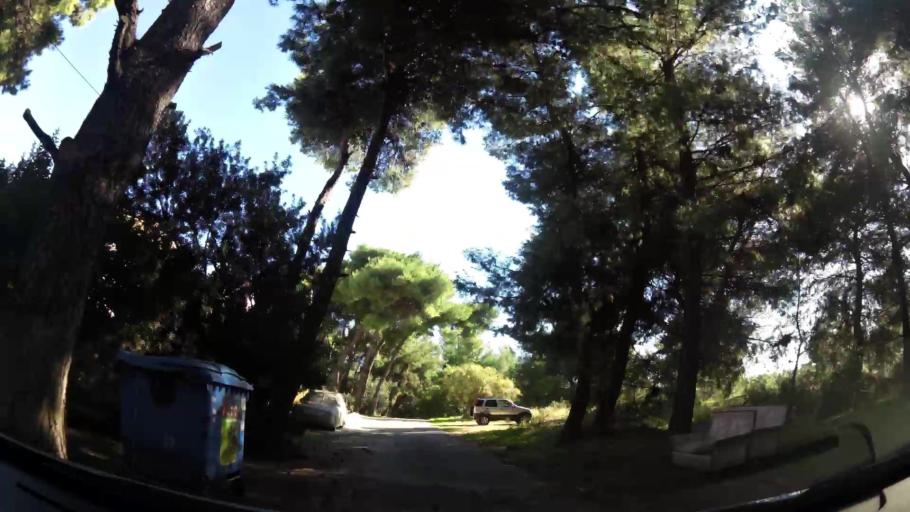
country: GR
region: Attica
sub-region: Nomarchia Athinas
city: Ekali
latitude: 38.1227
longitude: 23.8405
